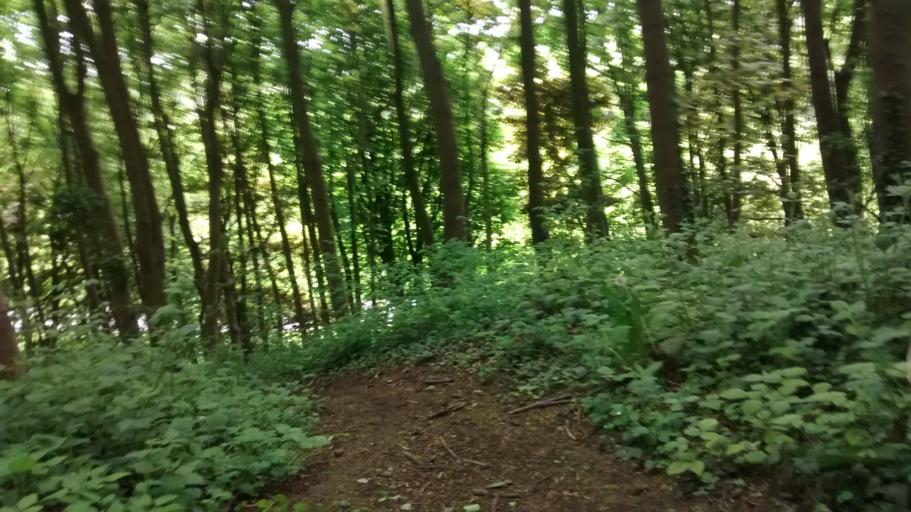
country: GB
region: England
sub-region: County Durham
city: Pittington
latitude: 54.7945
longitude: -1.4825
